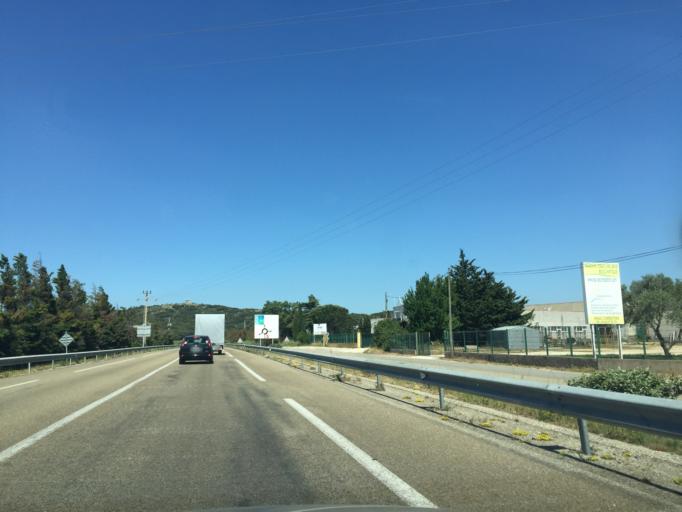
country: FR
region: Languedoc-Roussillon
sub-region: Departement du Gard
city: Saze
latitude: 43.9549
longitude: 4.6582
